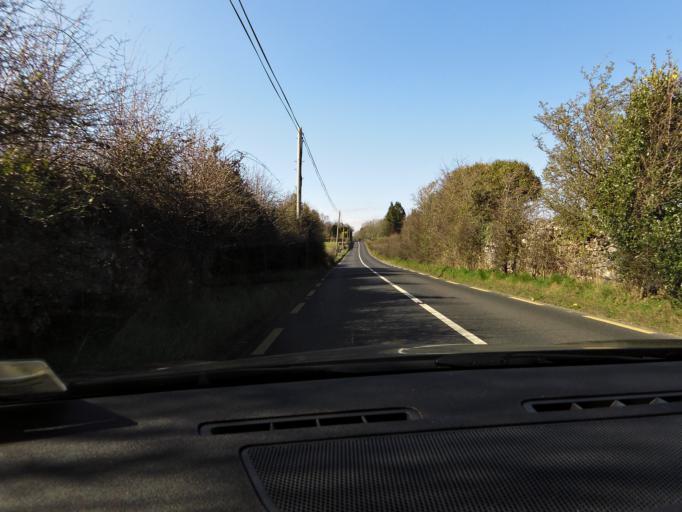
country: IE
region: Connaught
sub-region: County Galway
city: Oughterard
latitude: 53.4161
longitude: -9.2904
